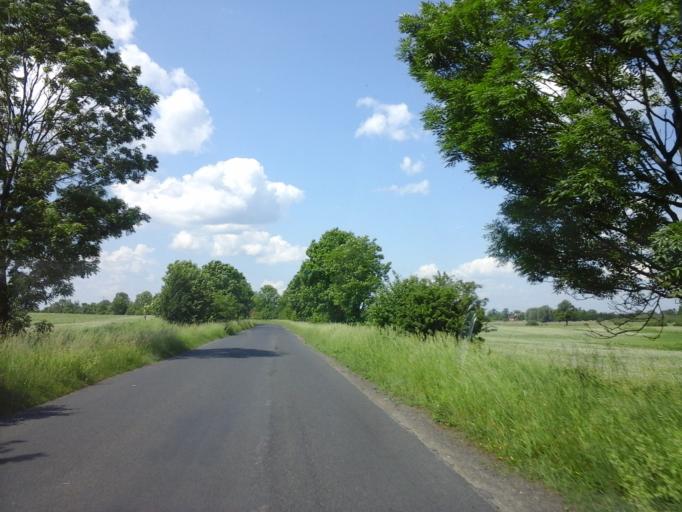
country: PL
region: West Pomeranian Voivodeship
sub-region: Powiat choszczenski
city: Bierzwnik
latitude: 53.0452
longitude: 15.6770
